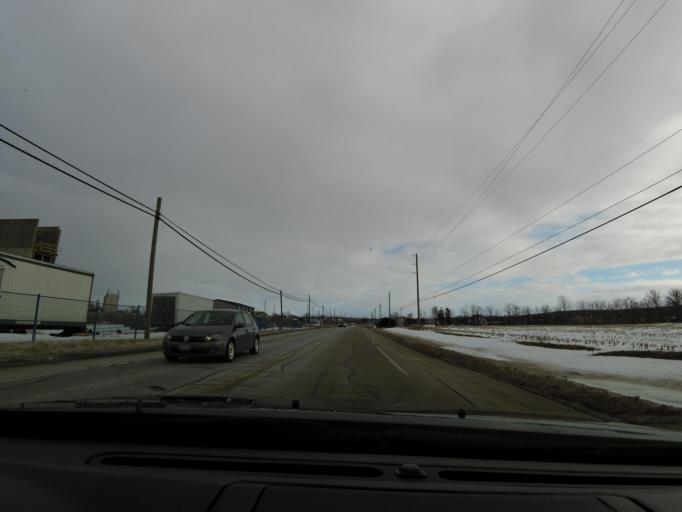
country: CA
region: Ontario
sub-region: Regional Municipality of Niagara
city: St. Catharines
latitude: 43.1829
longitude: -79.5126
